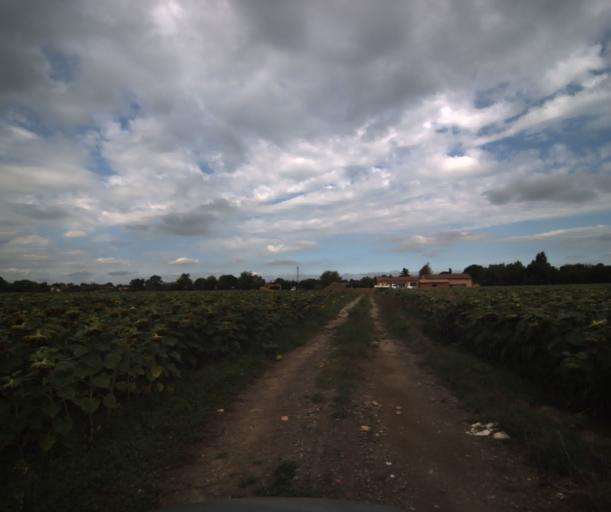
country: FR
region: Midi-Pyrenees
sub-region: Departement de la Haute-Garonne
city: Lacasse
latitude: 43.3998
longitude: 1.2616
